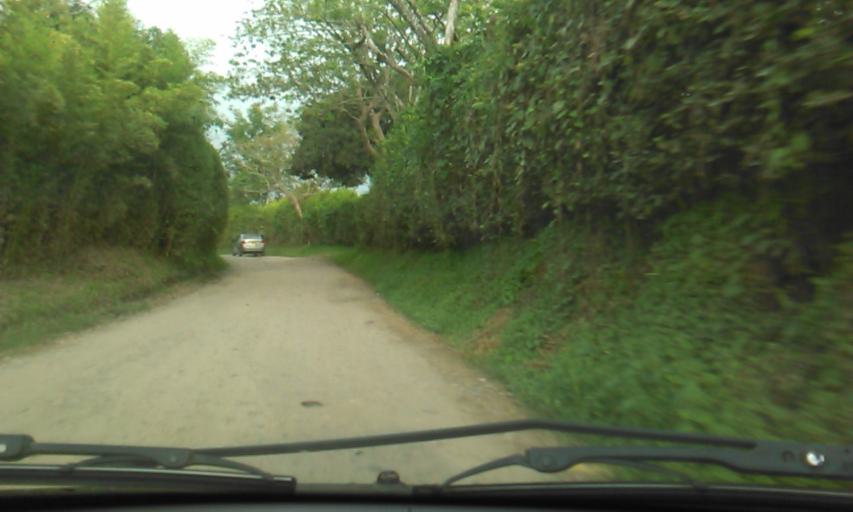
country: CO
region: Quindio
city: Montenegro
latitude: 4.5450
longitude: -75.7348
